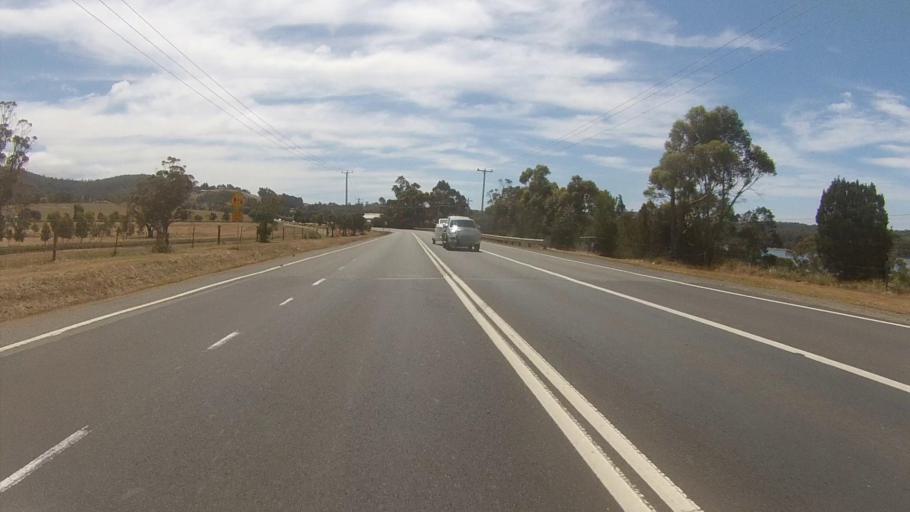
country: AU
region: Tasmania
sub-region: Kingborough
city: Margate
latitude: -43.0173
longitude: 147.2705
